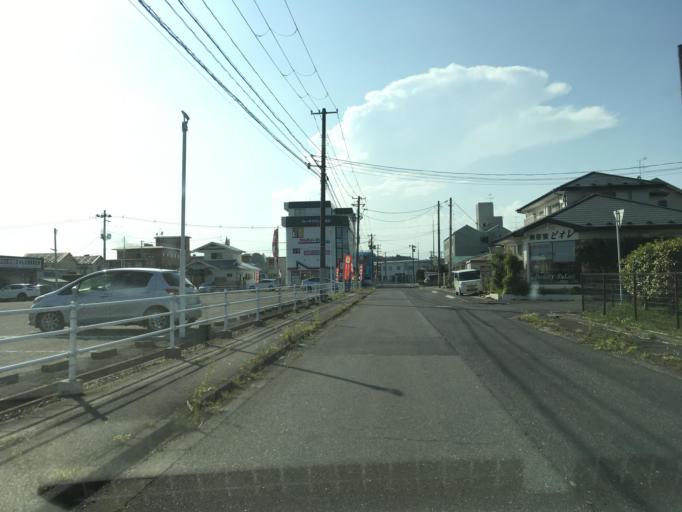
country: JP
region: Miyagi
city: Wakuya
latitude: 38.6895
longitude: 141.1857
